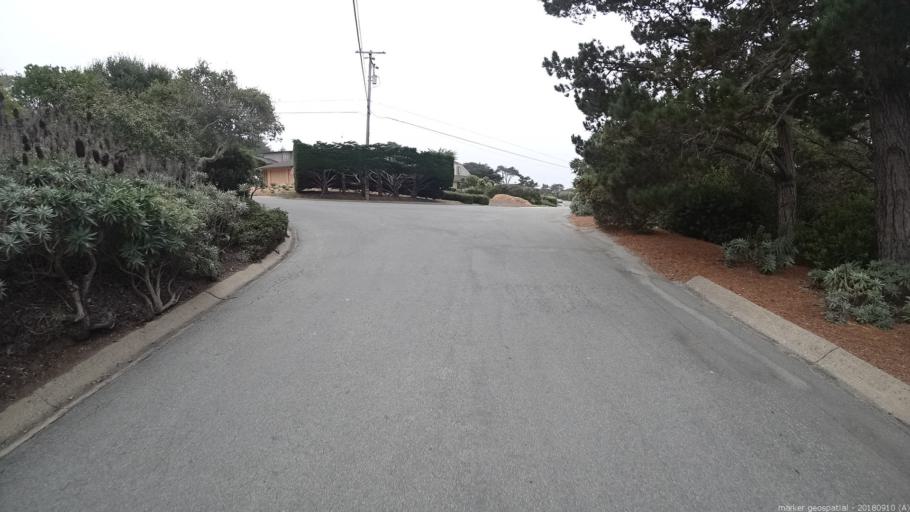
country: US
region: California
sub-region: Monterey County
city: Carmel-by-the-Sea
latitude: 36.4868
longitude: -121.9395
